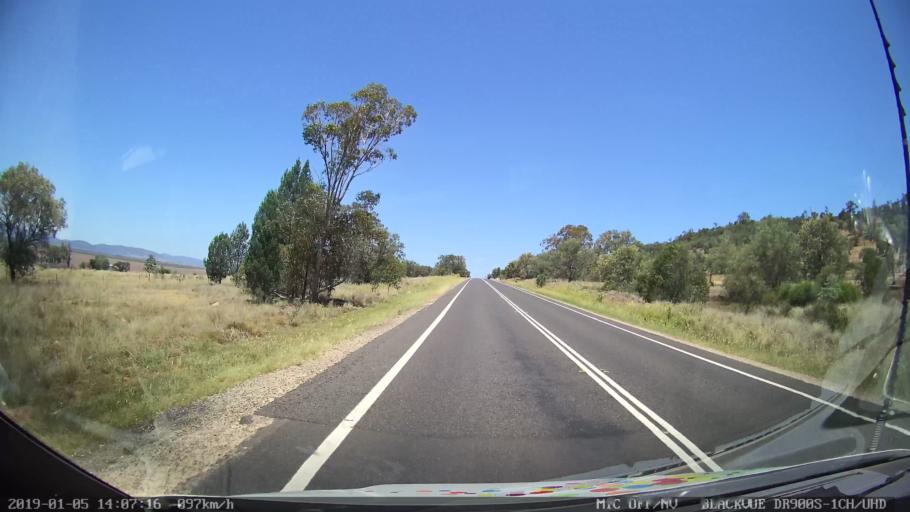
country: AU
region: New South Wales
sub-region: Gunnedah
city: Gunnedah
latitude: -31.2209
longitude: 150.4044
